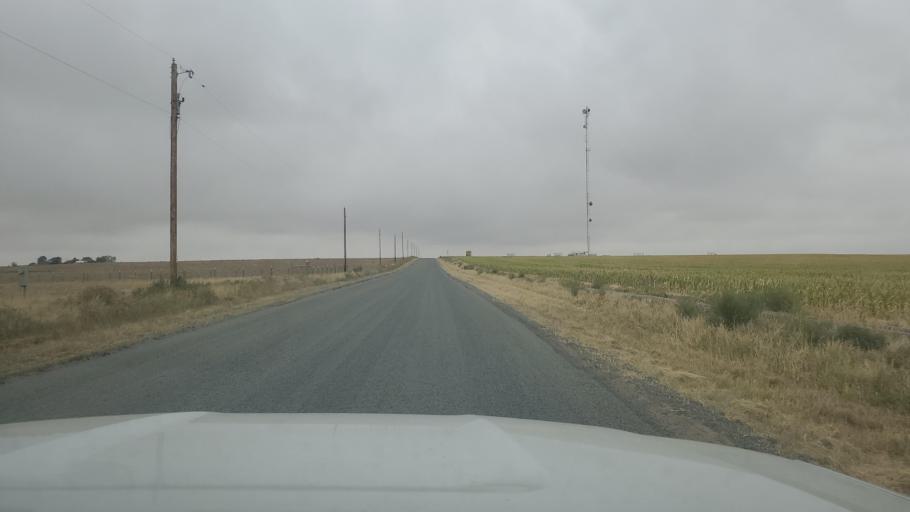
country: US
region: Colorado
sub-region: Weld County
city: Lochbuie
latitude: 39.9208
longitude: -104.6027
